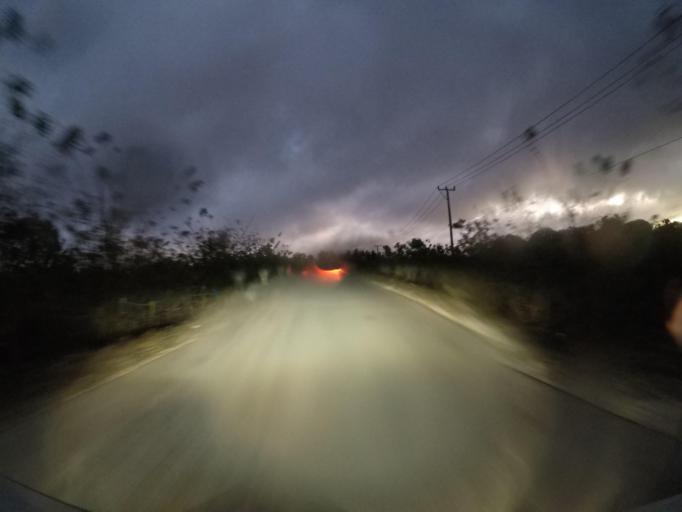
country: TL
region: Lautem
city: Lospalos
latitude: -8.4274
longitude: 127.0036
